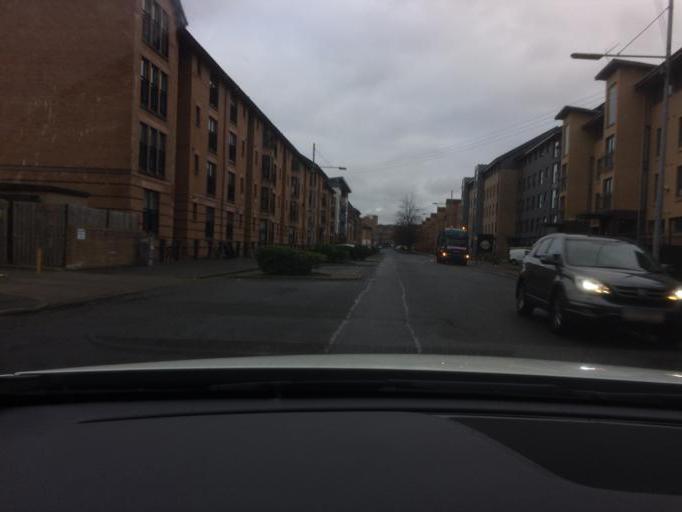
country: GB
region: Scotland
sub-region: Glasgow City
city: Glasgow
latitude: 55.8642
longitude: -4.2926
